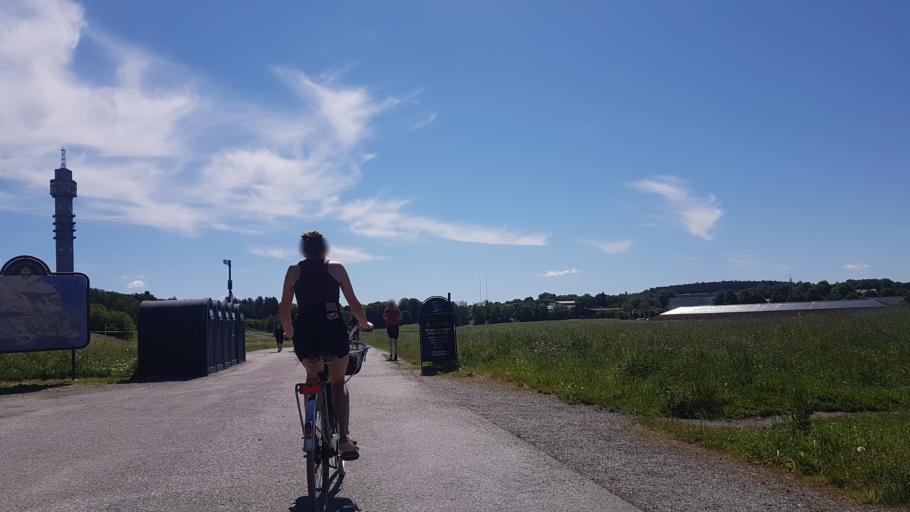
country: SE
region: Stockholm
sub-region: Stockholms Kommun
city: OEstermalm
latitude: 59.3375
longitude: 18.1153
